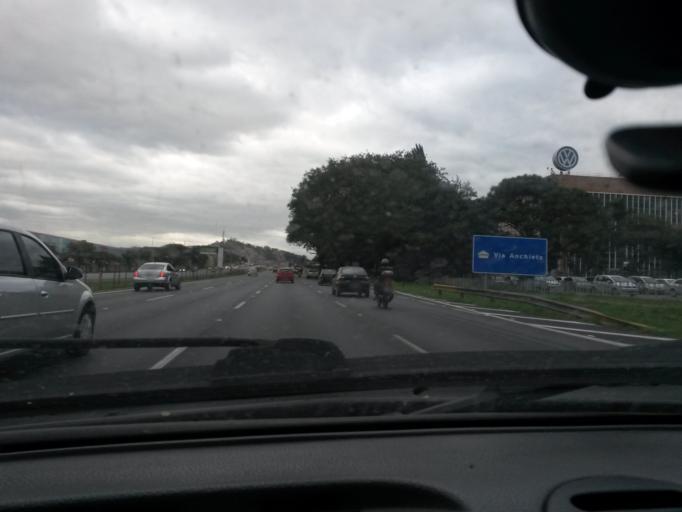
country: BR
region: Sao Paulo
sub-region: Sao Bernardo Do Campo
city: Sao Bernardo do Campo
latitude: -23.7286
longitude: -46.5490
